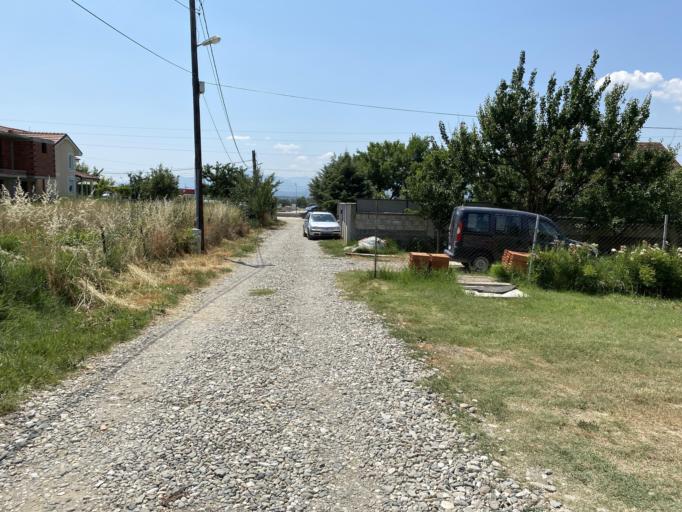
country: MK
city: Radishani
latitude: 42.0472
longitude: 21.4453
